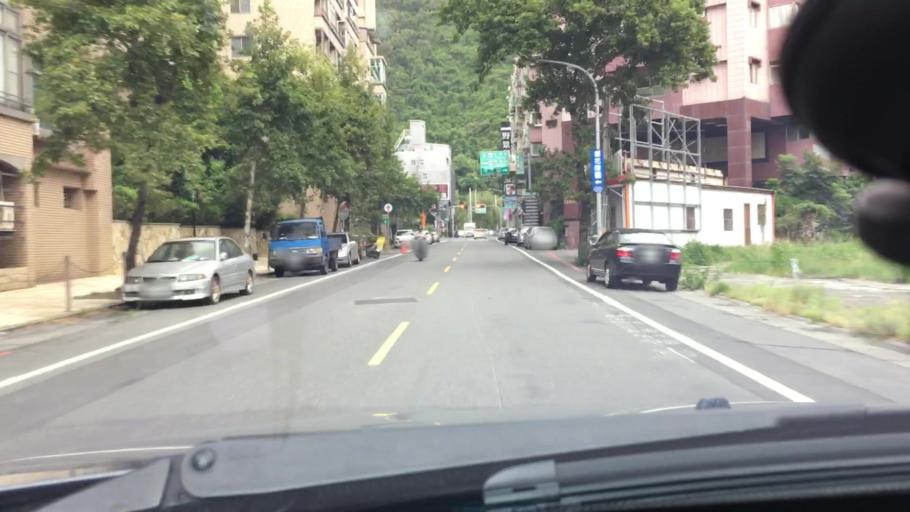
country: TW
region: Taiwan
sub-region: Yilan
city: Yilan
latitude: 24.8247
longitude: 121.7642
